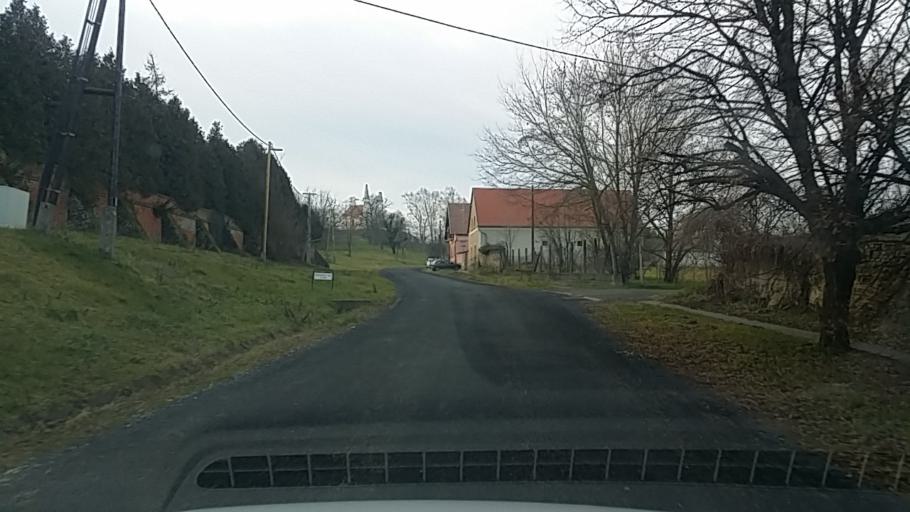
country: HU
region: Vas
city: Sarvar
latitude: 47.2376
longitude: 17.0170
